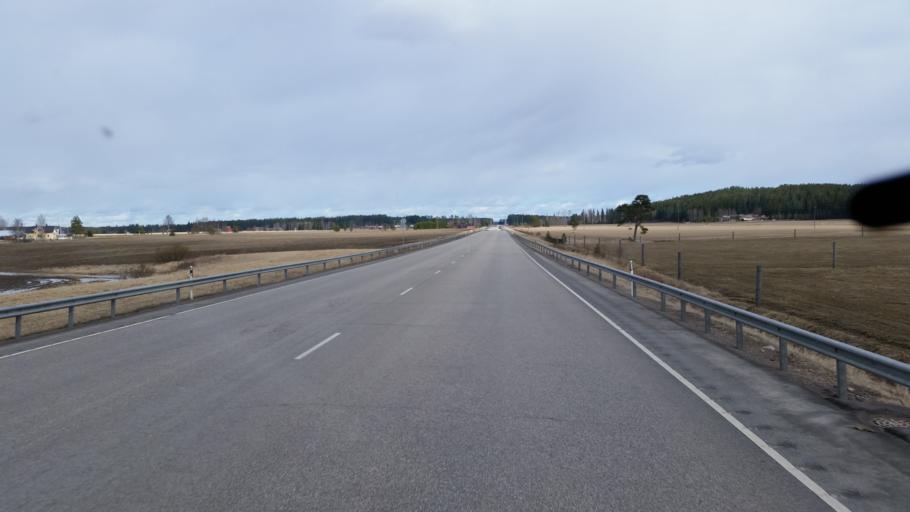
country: FI
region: Kymenlaakso
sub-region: Kouvola
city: Elimaeki
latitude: 60.7624
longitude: 26.4684
